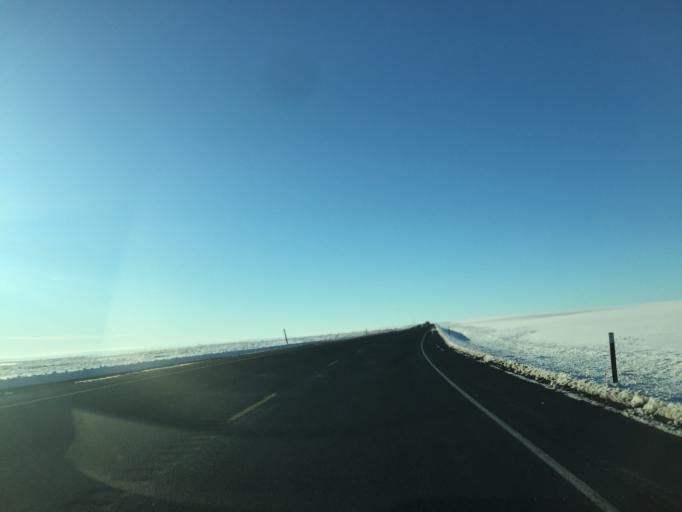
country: US
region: Washington
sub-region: Okanogan County
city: Coulee Dam
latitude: 47.6845
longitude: -118.9875
